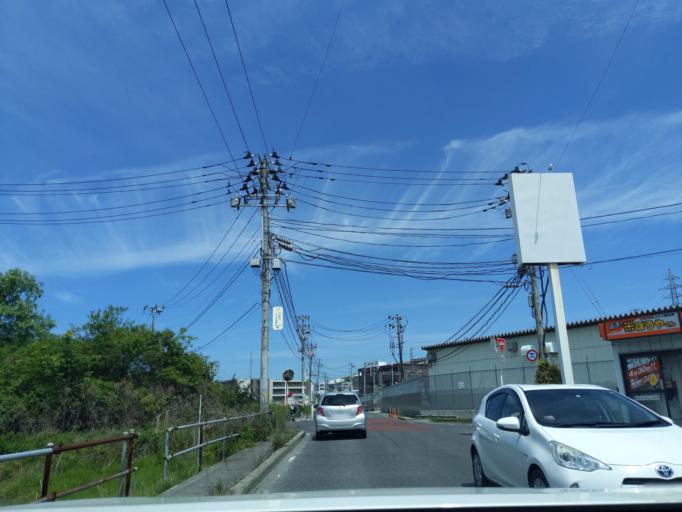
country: JP
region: Fukushima
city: Koriyama
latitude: 37.4112
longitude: 140.3789
